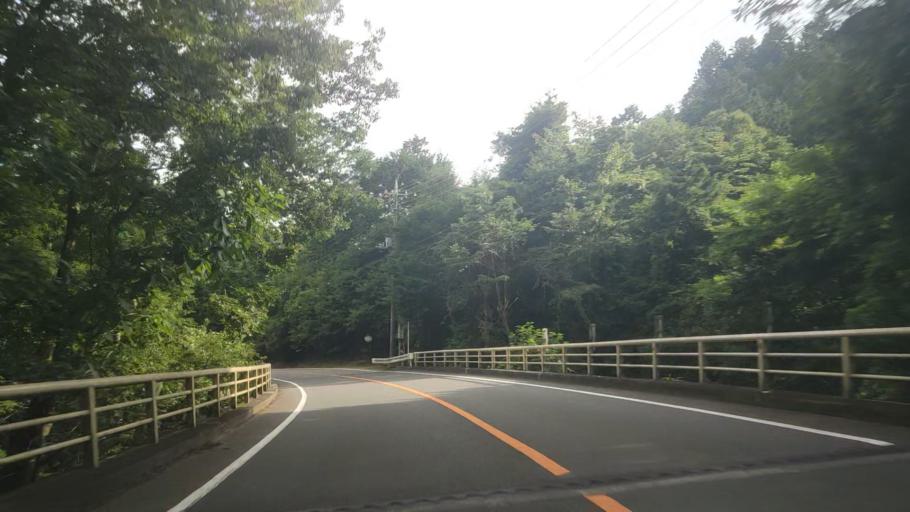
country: JP
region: Gunma
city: Kiryu
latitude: 36.5960
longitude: 139.4035
